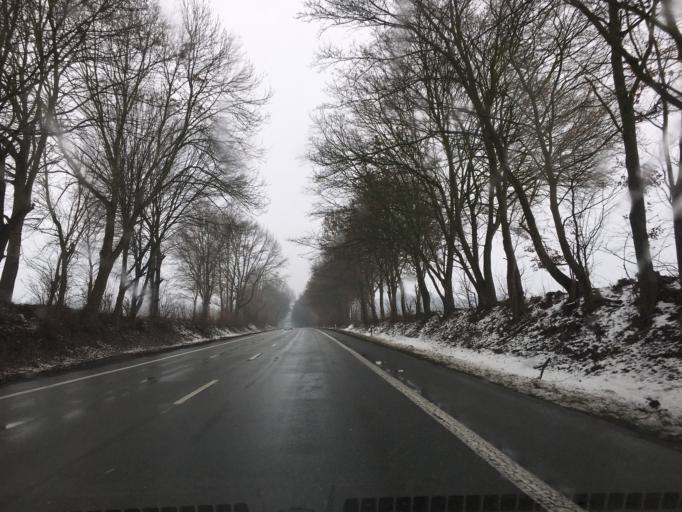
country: DE
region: North Rhine-Westphalia
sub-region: Regierungsbezirk Munster
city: Klein Reken
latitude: 51.7925
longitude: 7.0300
